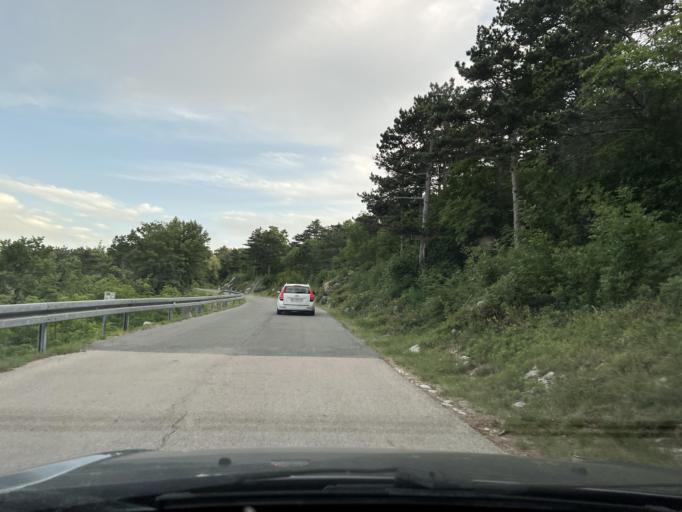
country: HR
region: Primorsko-Goranska
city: Marcelji
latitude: 45.3891
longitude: 14.4176
